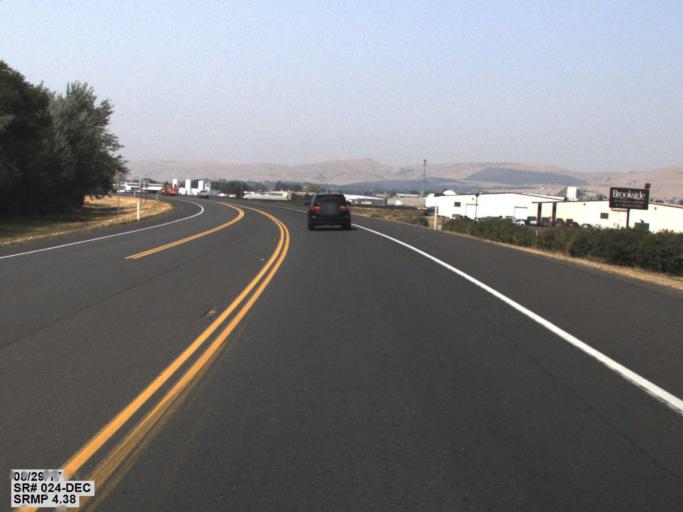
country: US
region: Washington
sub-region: Yakima County
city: Terrace Heights
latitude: 46.5575
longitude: -120.3941
